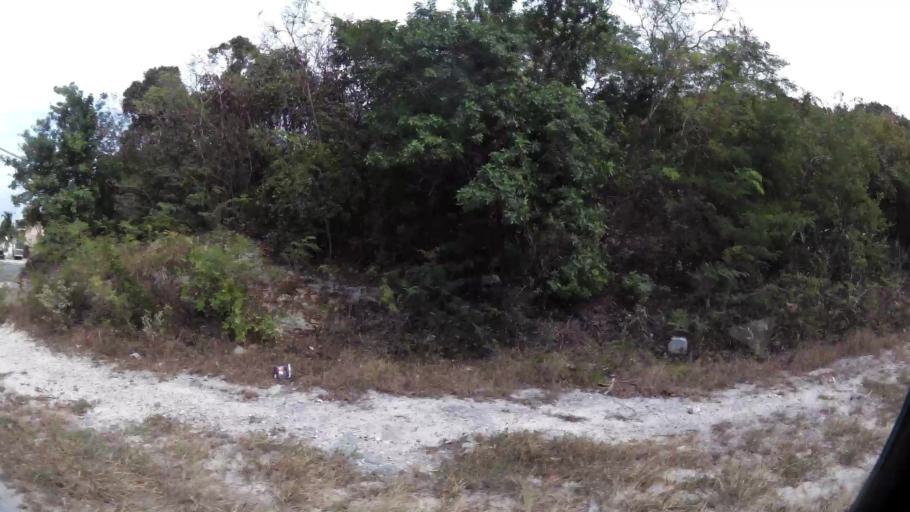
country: BS
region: Mayaguana
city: Abraham's Bay
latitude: 21.7836
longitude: -72.2278
